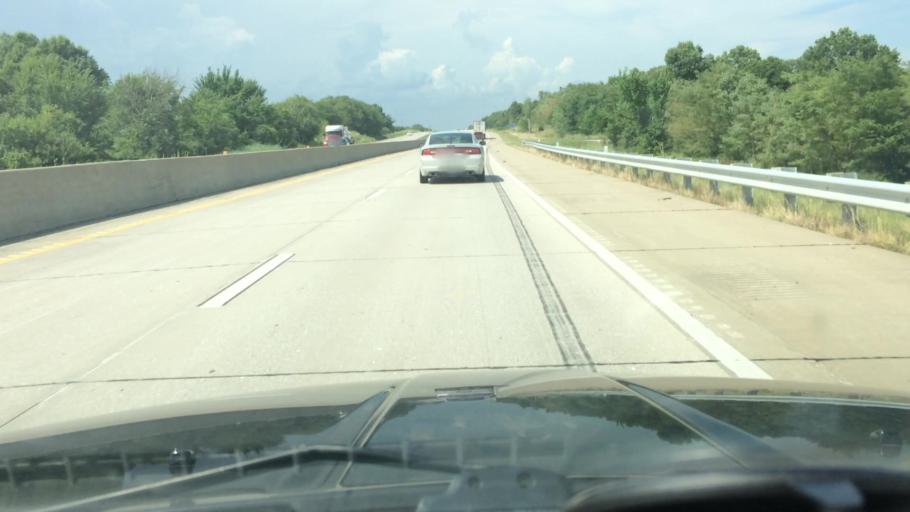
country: US
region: Missouri
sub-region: Henry County
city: Clinton
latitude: 38.2922
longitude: -93.7591
